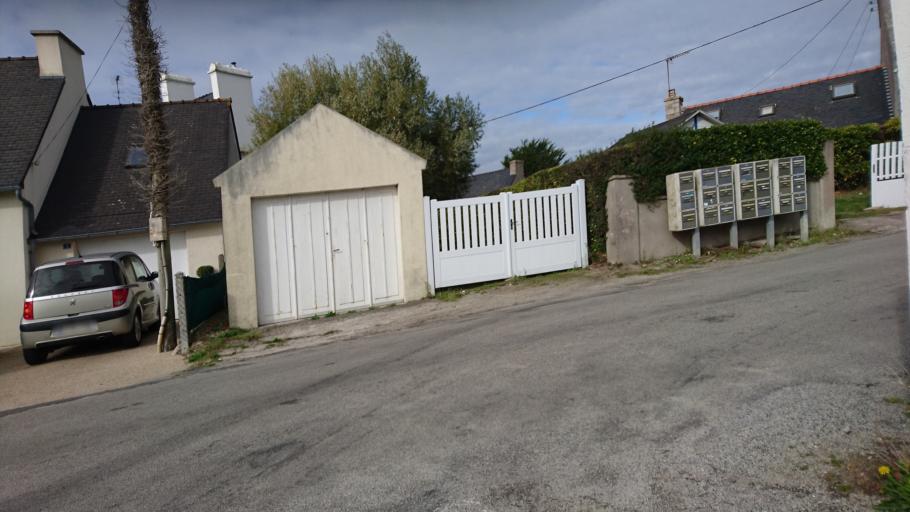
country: FR
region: Brittany
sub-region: Departement du Finistere
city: Lampaul-Plouarzel
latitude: 48.4480
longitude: -4.7678
